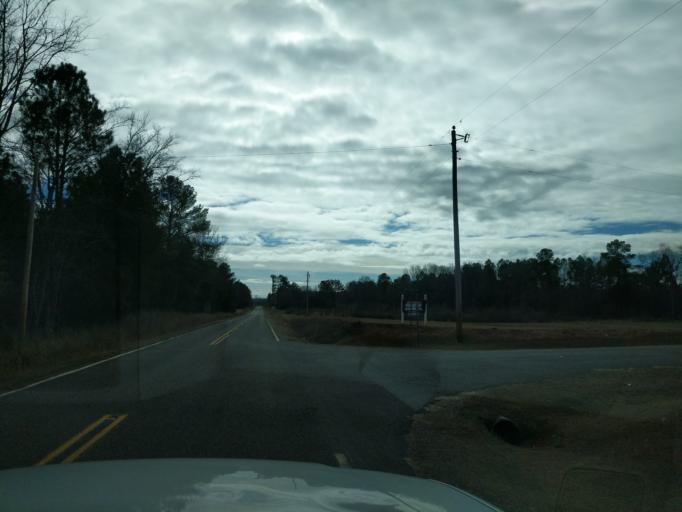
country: US
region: South Carolina
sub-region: Edgefield County
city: Edgefield
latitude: 33.9262
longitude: -82.0081
